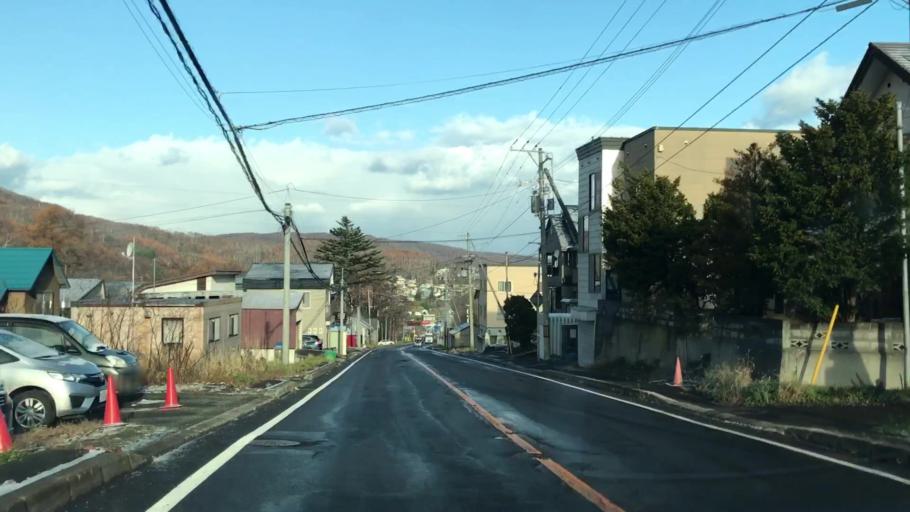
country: JP
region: Hokkaido
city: Otaru
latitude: 43.1630
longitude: 140.9979
